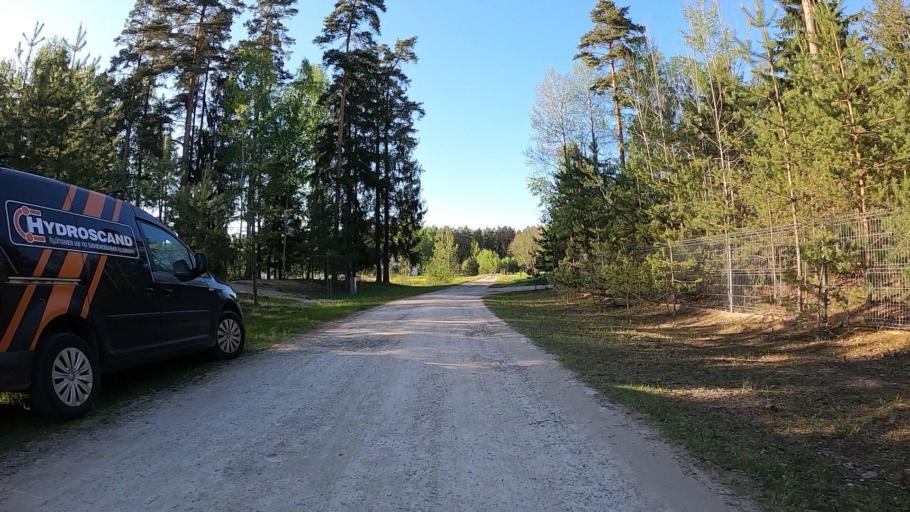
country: LV
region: Baldone
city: Baldone
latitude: 56.7765
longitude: 24.3090
